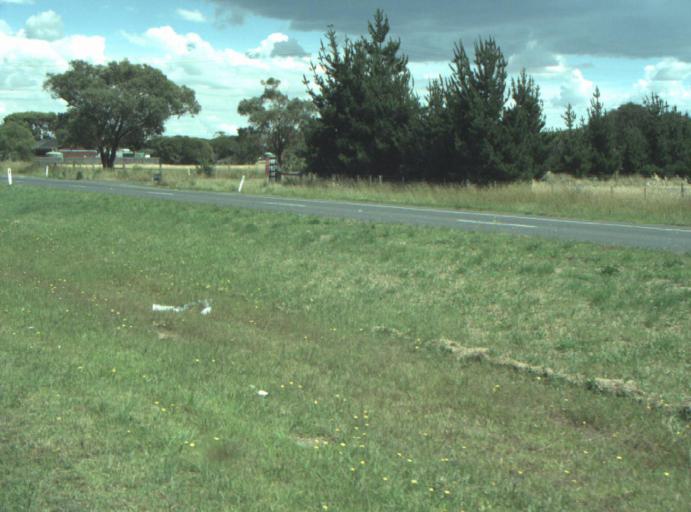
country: AU
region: Victoria
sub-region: Greater Geelong
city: Leopold
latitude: -38.1740
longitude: 144.4544
